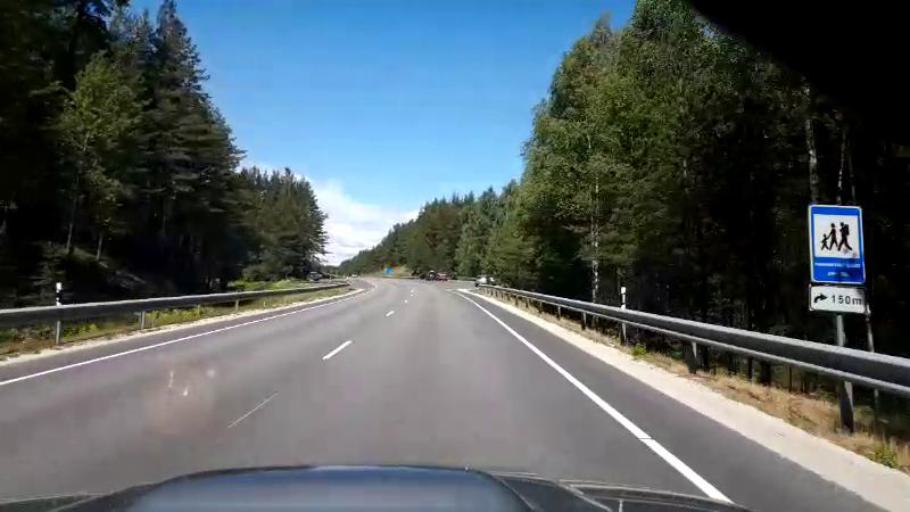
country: EE
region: Paernumaa
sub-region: Paernu linn
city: Parnu
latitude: 58.1357
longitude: 24.5106
